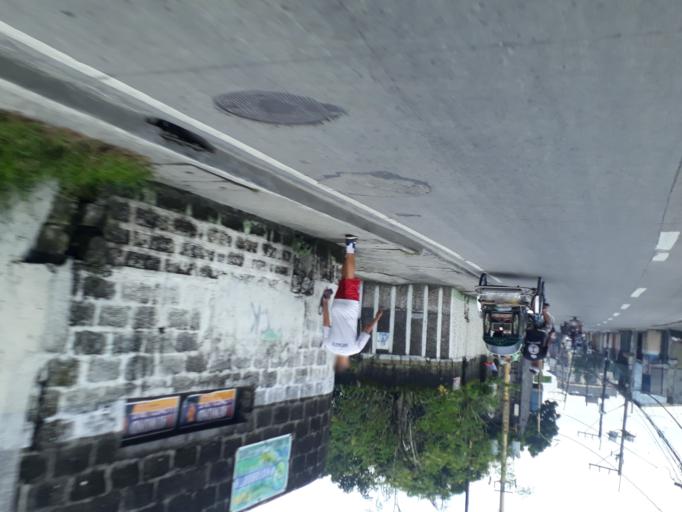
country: PH
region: Calabarzon
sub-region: Province of Rizal
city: Navotas
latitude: 14.6669
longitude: 120.9439
